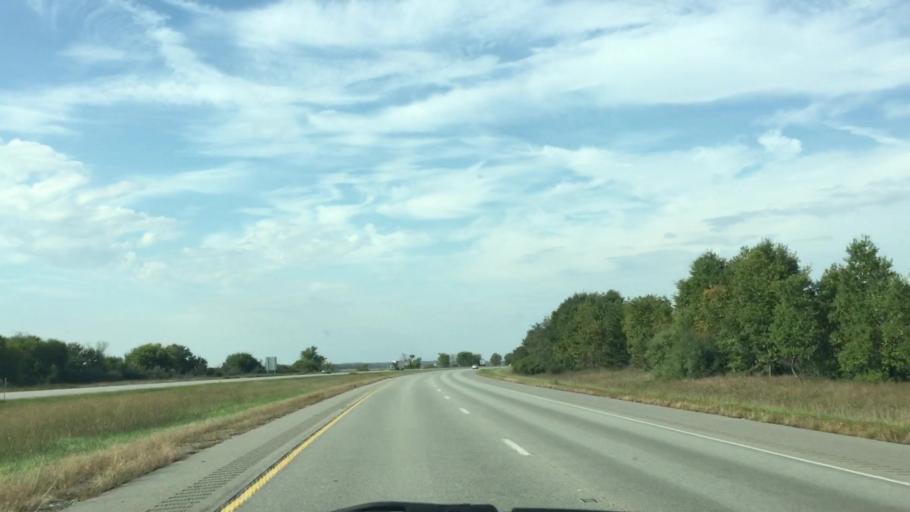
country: US
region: Illinois
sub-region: Rock Island County
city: Port Byron
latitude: 41.5463
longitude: -90.2559
